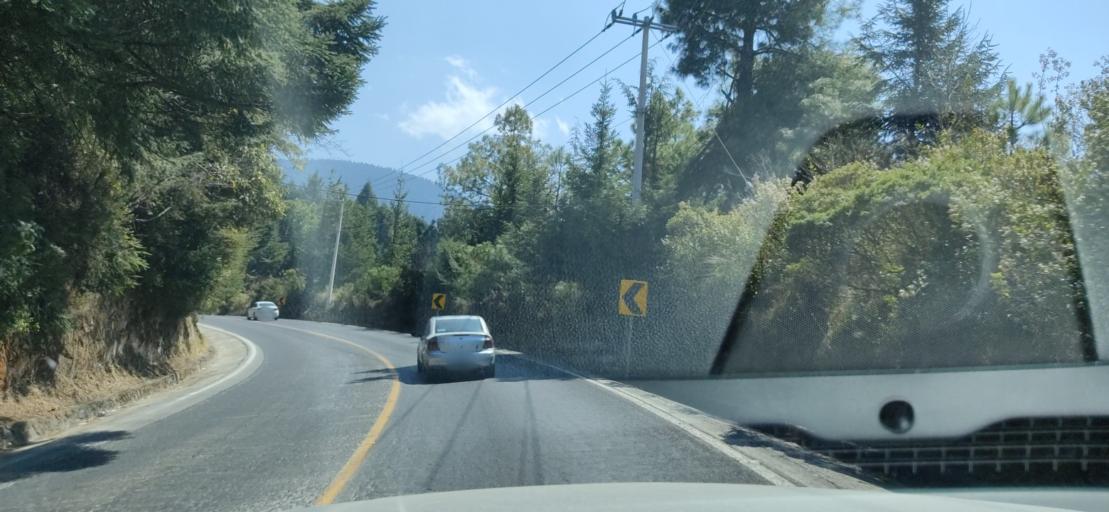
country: MX
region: Mexico
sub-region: Ocoyoacac
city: San Jeronimo Acazulco
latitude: 19.2642
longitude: -99.3763
